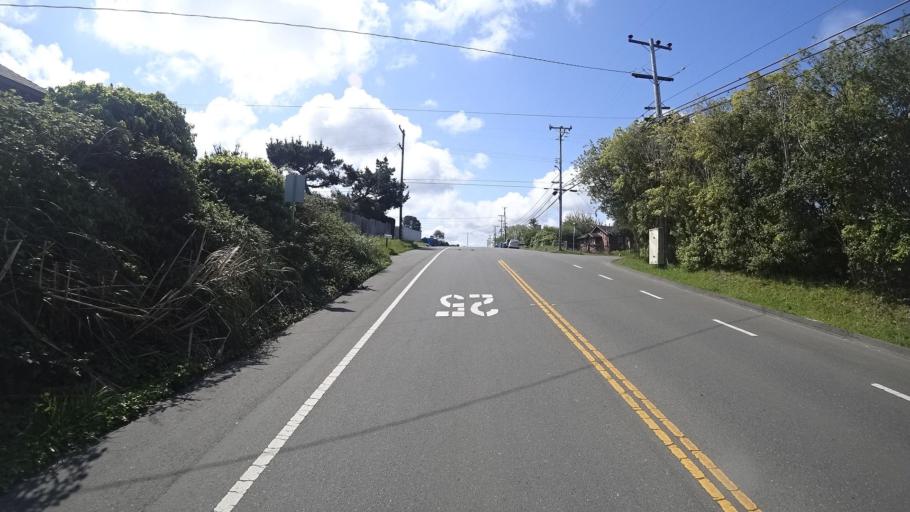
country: US
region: California
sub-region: Humboldt County
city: Bayview
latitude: 40.7664
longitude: -124.1755
